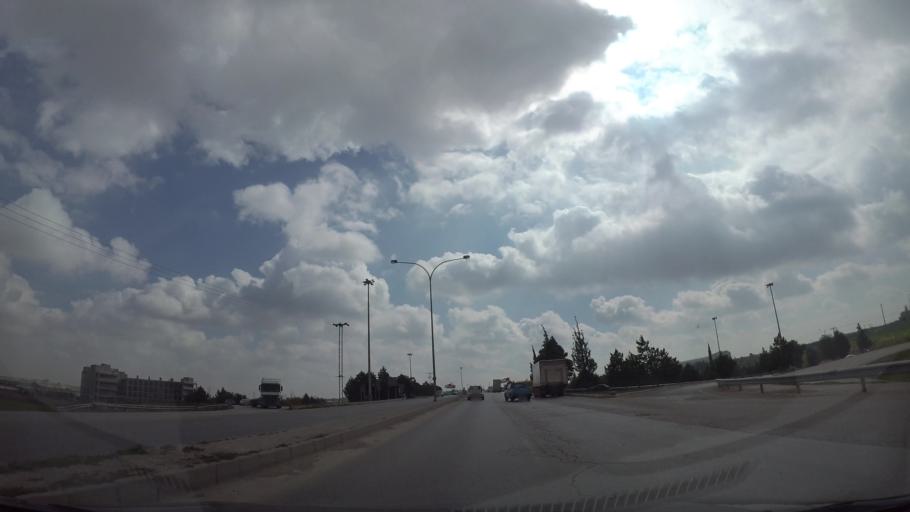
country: JO
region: Amman
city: Jawa
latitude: 31.8152
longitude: 35.9088
